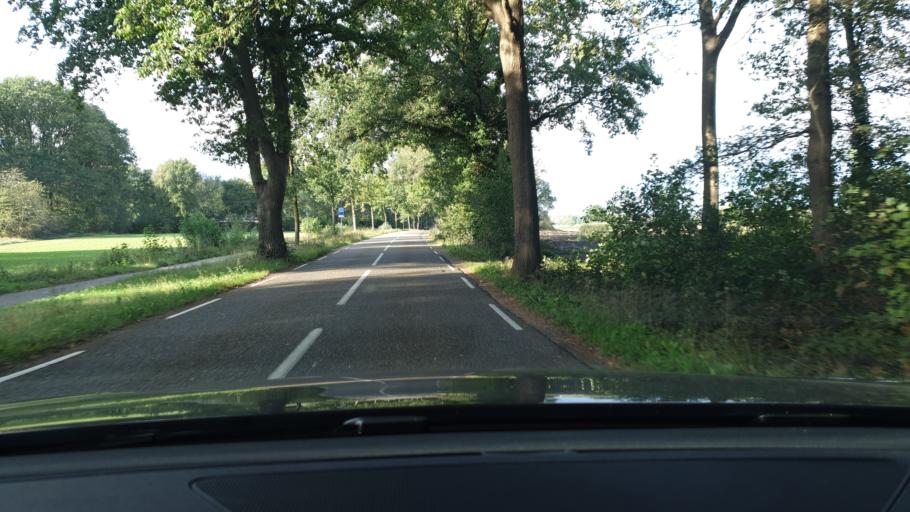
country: NL
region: Limburg
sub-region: Gemeente Venlo
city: Arcen
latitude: 51.4745
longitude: 6.1659
